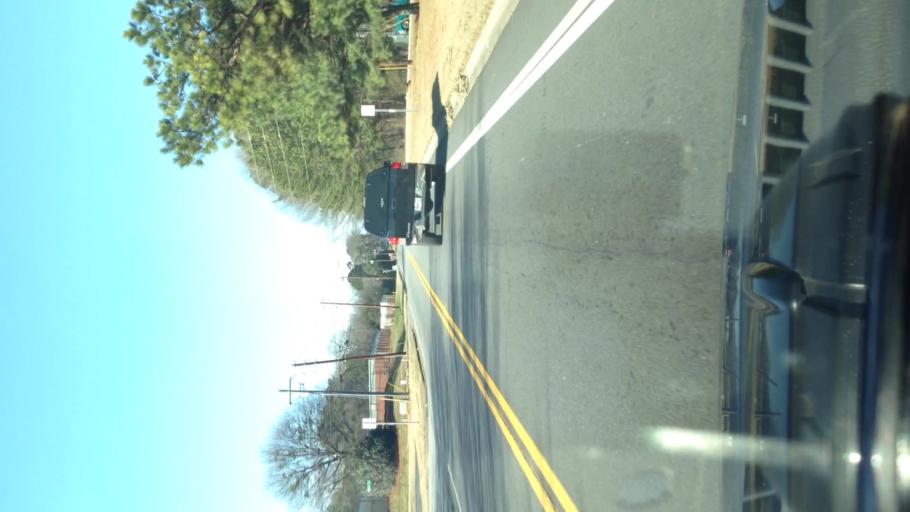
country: US
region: Georgia
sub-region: Gwinnett County
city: Norcross
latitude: 33.9171
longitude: -84.2398
